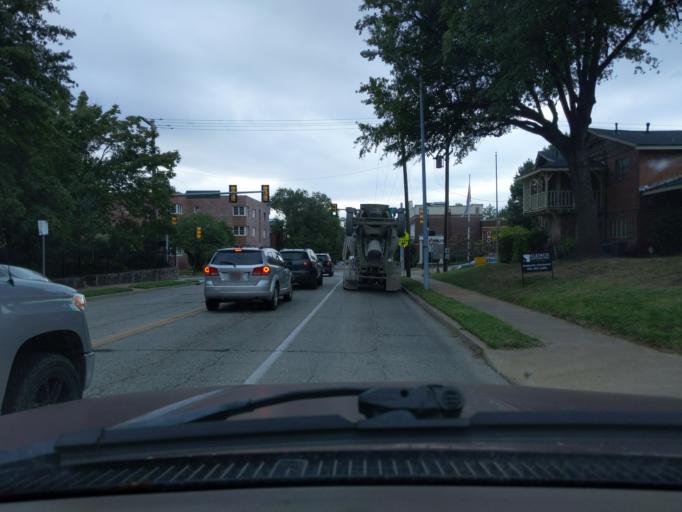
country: US
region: Oklahoma
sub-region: Tulsa County
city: Tulsa
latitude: 36.1334
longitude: -95.9829
